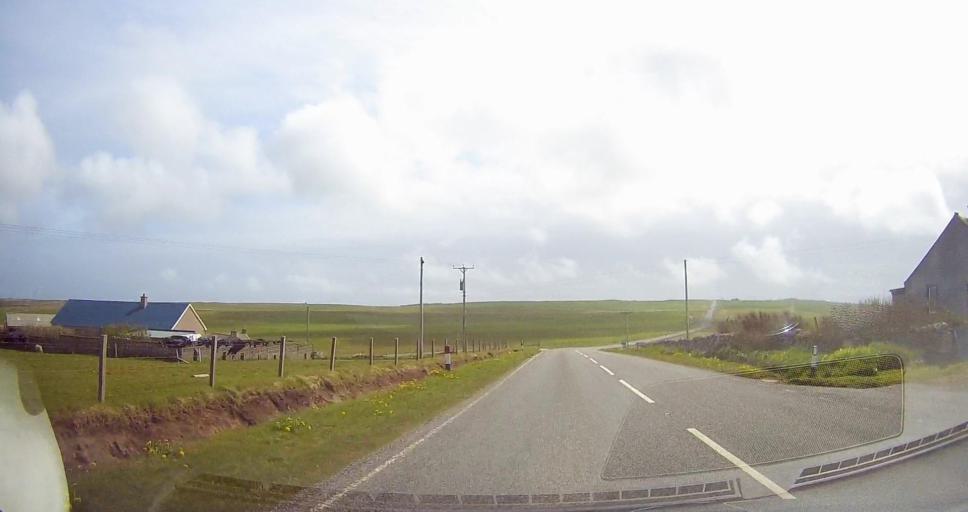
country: GB
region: Scotland
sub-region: Shetland Islands
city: Sandwick
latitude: 59.9117
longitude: -1.3019
